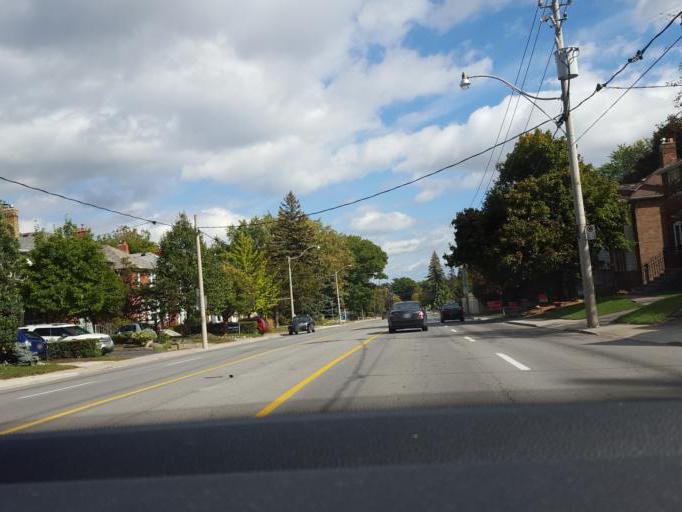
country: CA
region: Ontario
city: Toronto
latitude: 43.7274
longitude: -79.3912
